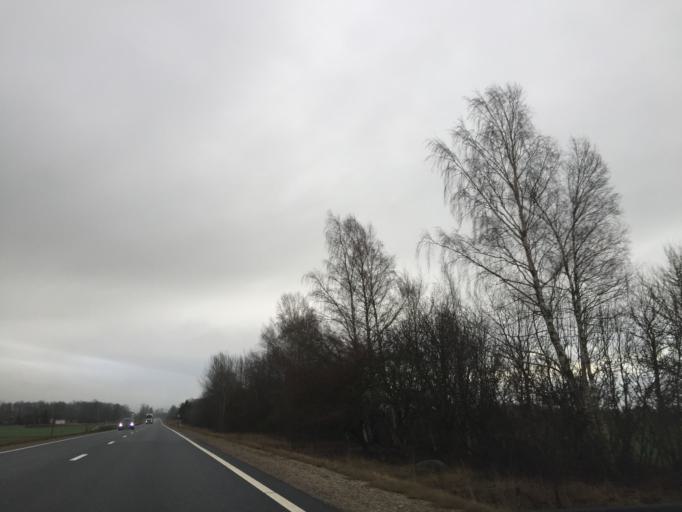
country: LV
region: Durbe
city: Liegi
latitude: 56.5902
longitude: 21.4121
